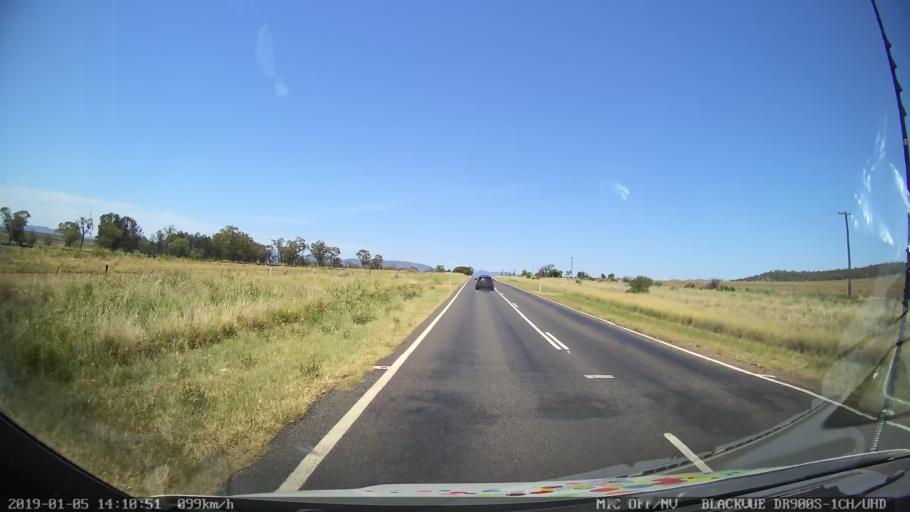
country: AU
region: New South Wales
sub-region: Gunnedah
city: Gunnedah
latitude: -31.2448
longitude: 150.4493
